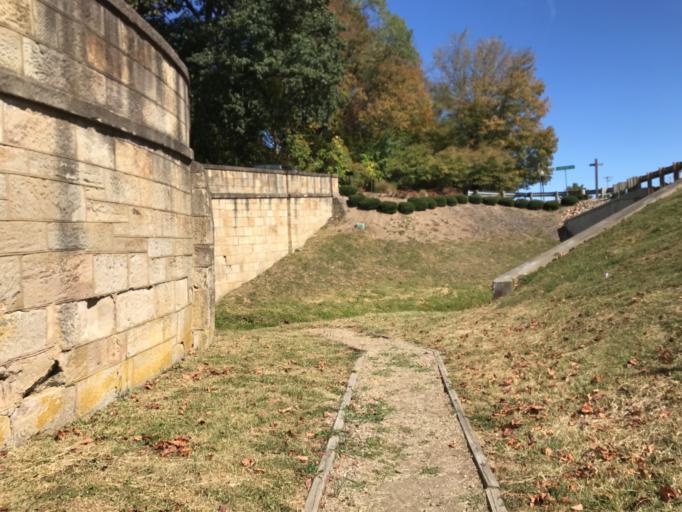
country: US
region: Ohio
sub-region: Muskingum County
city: New Concord
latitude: 39.9928
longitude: -81.7464
